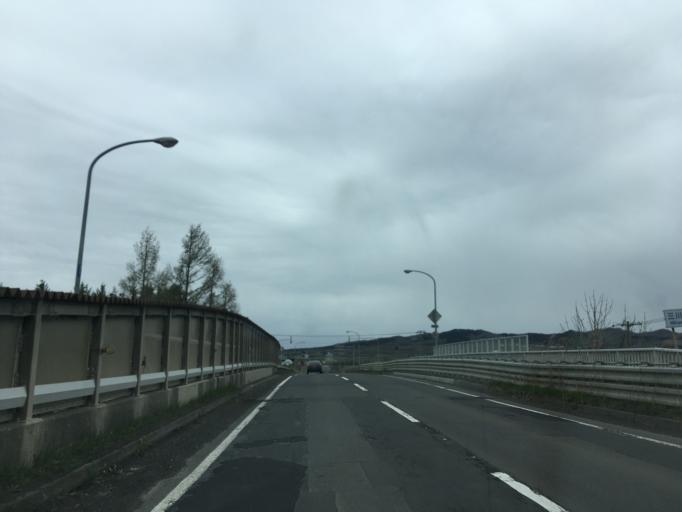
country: JP
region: Hokkaido
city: Chitose
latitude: 42.9497
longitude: 141.8003
